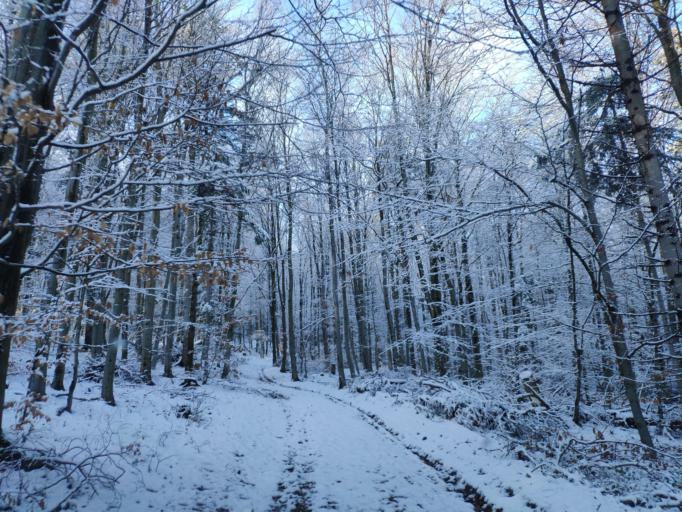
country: SK
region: Kosicky
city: Moldava nad Bodvou
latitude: 48.7441
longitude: 21.0874
